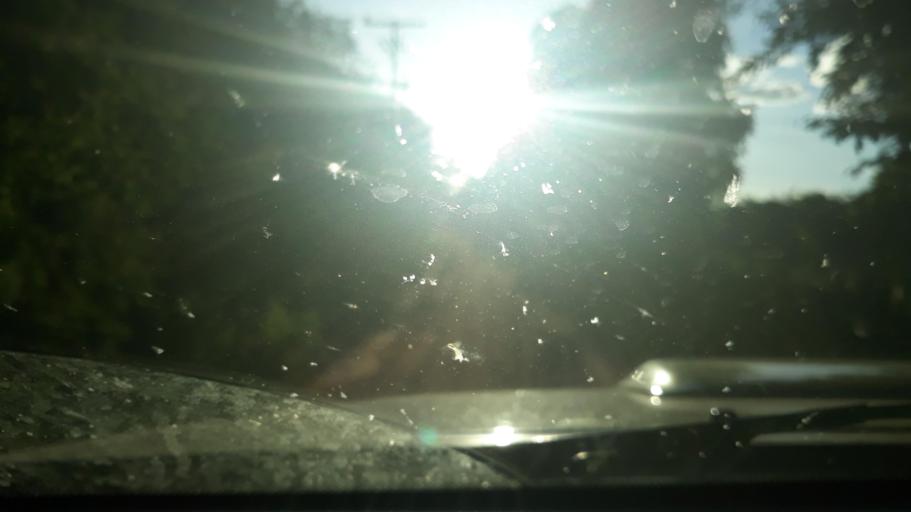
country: BR
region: Bahia
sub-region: Riacho De Santana
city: Riacho de Santana
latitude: -13.8472
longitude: -42.7463
